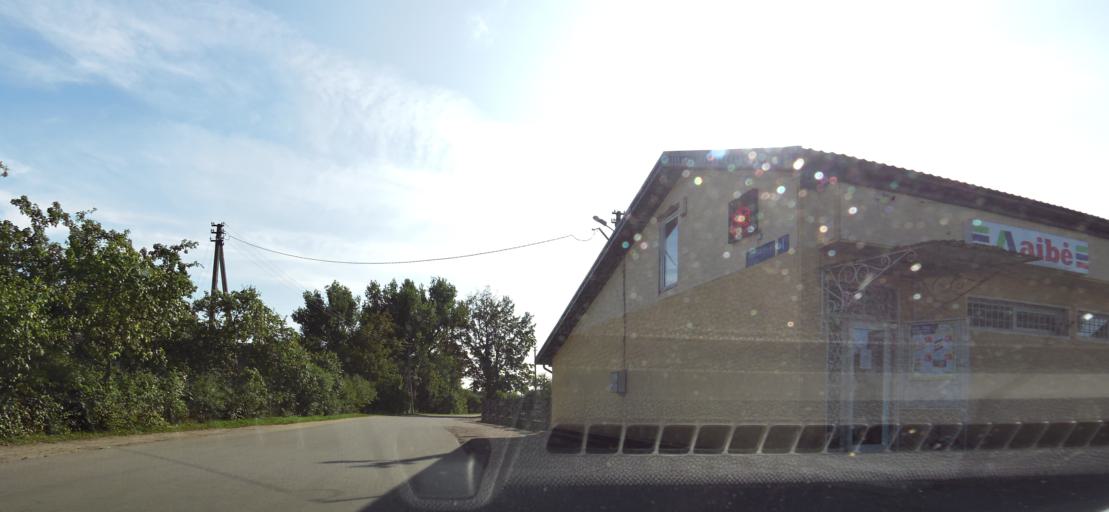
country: LT
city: Salcininkai
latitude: 54.4401
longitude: 25.3128
